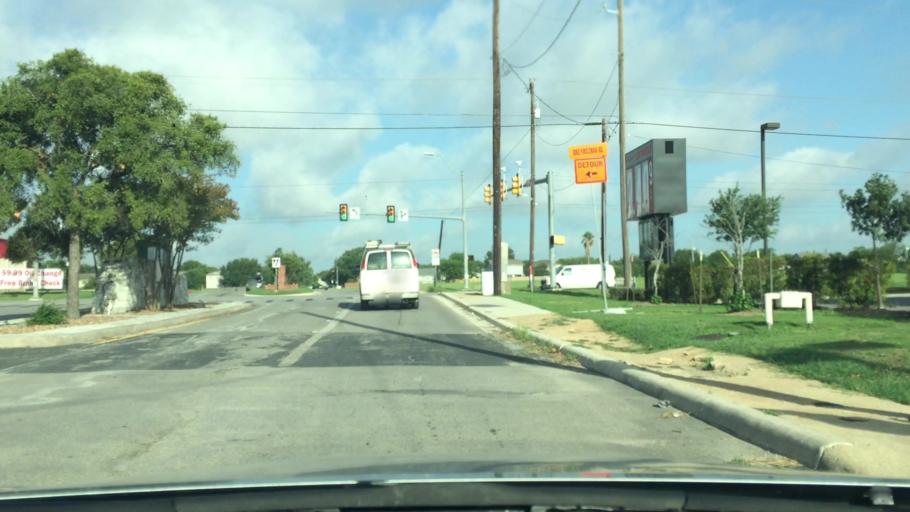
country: US
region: Texas
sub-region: Bexar County
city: Kirby
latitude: 29.4678
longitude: -98.3588
